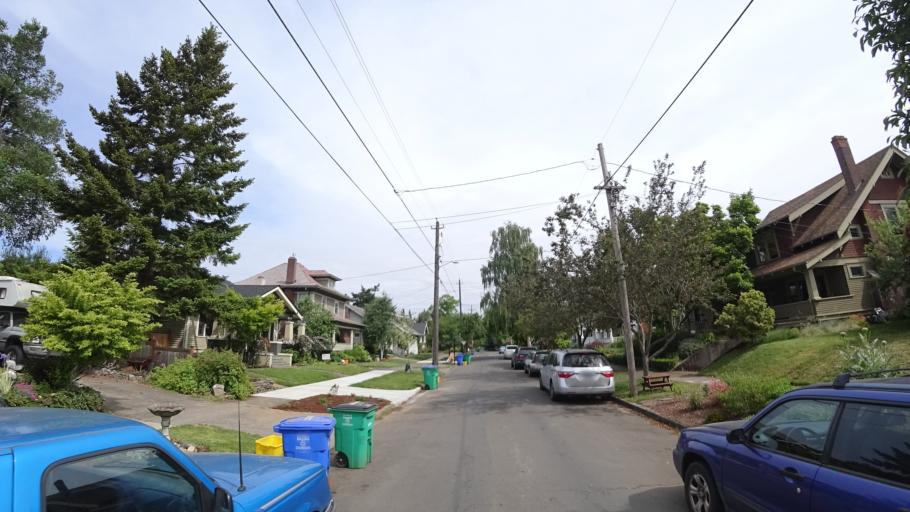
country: US
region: Oregon
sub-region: Multnomah County
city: Portland
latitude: 45.5356
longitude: -122.6120
